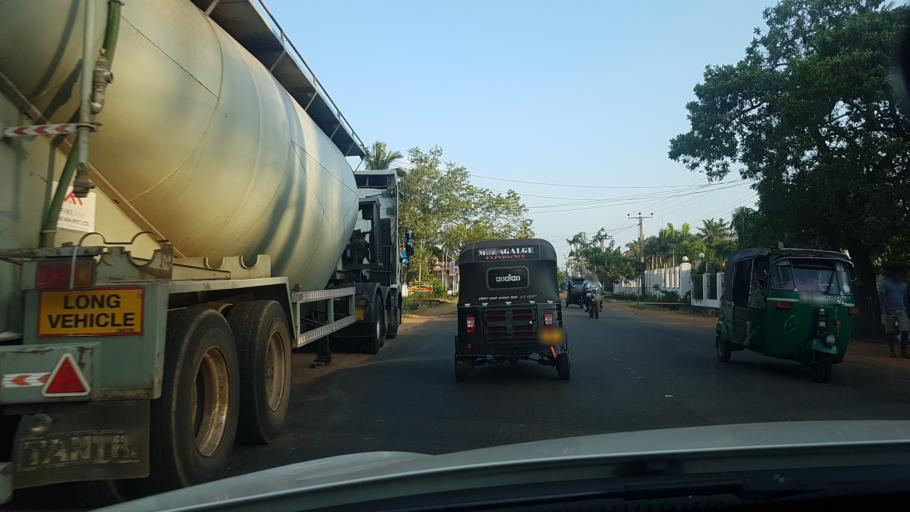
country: LK
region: North Western
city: Chilaw
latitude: 7.5669
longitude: 79.8007
